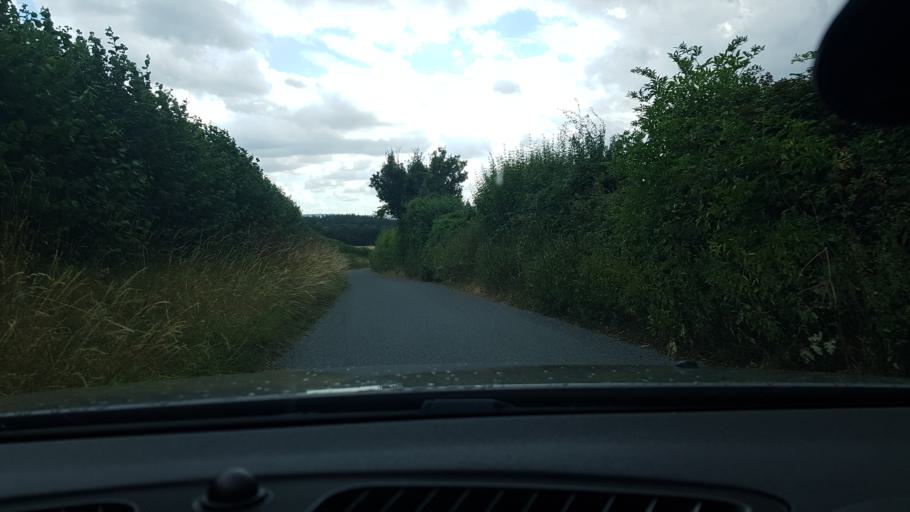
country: GB
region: England
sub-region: West Berkshire
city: Wickham
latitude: 51.4358
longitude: -1.4380
